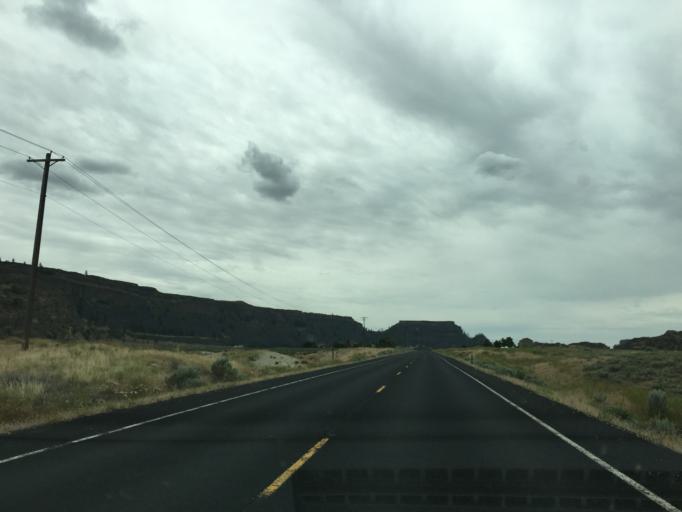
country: US
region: Washington
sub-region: Okanogan County
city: Coulee Dam
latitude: 47.9083
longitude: -119.0622
